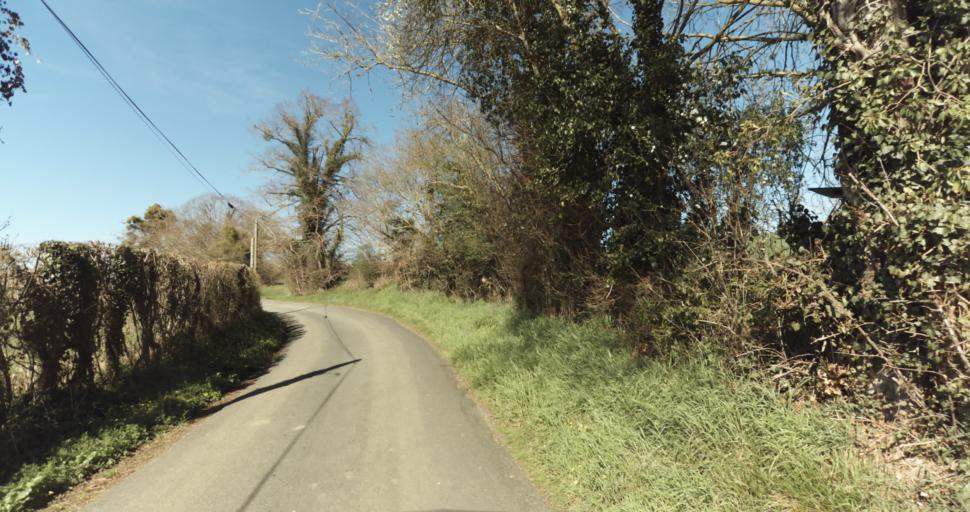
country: FR
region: Lower Normandy
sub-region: Departement du Calvados
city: Saint-Pierre-sur-Dives
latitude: 49.0660
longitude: -0.0317
